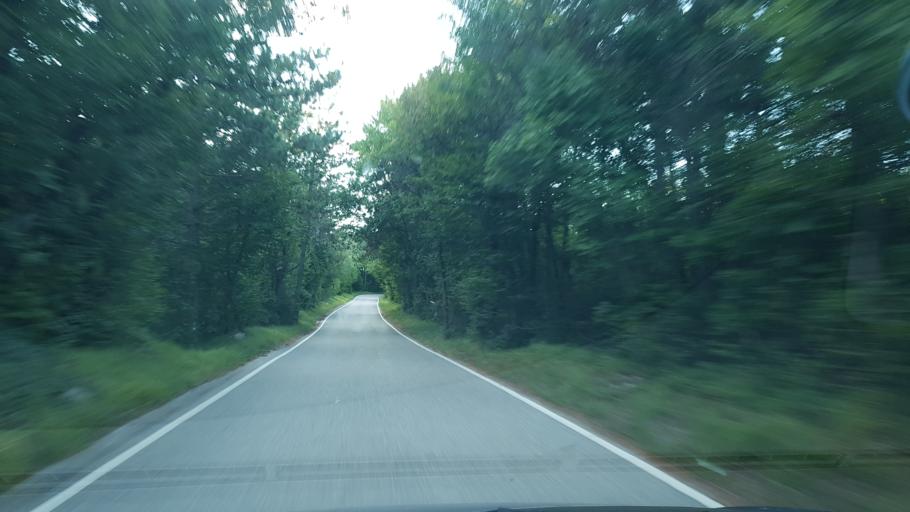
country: SI
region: Rence-Vogrsko
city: Rence
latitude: 45.8542
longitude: 13.6725
